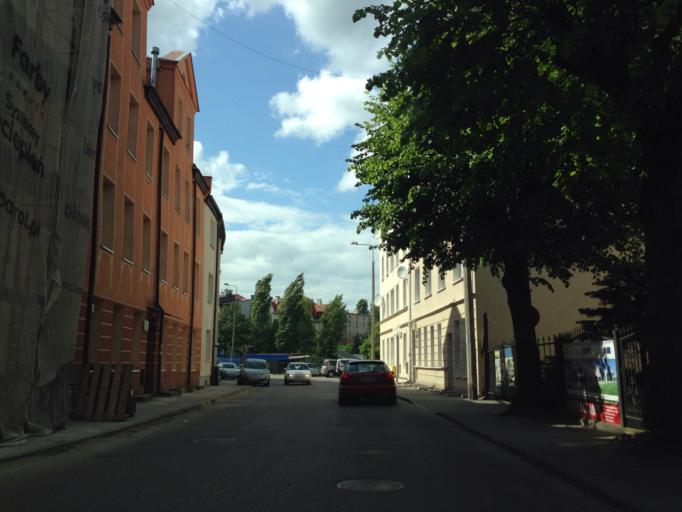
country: PL
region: Pomeranian Voivodeship
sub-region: Gdansk
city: Gdansk
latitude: 54.3794
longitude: 18.6188
